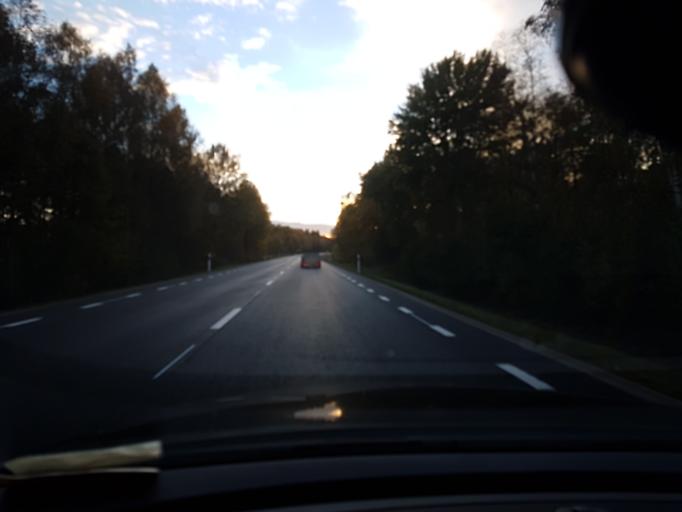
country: SE
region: Kronoberg
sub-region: Ljungby Kommun
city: Ljungby
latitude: 56.7592
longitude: 13.7672
